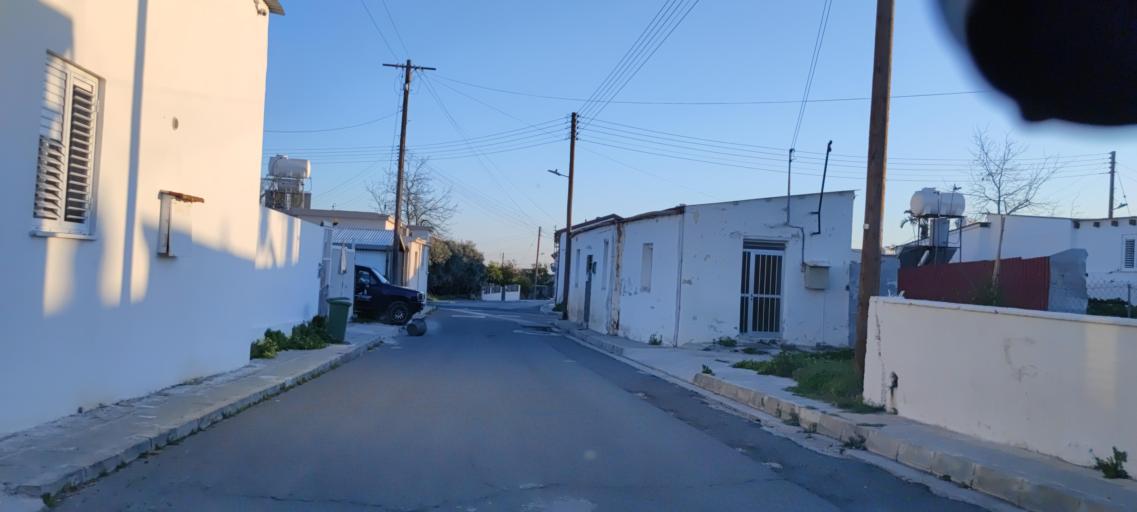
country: CY
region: Pafos
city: Paphos
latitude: 34.7832
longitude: 32.4185
